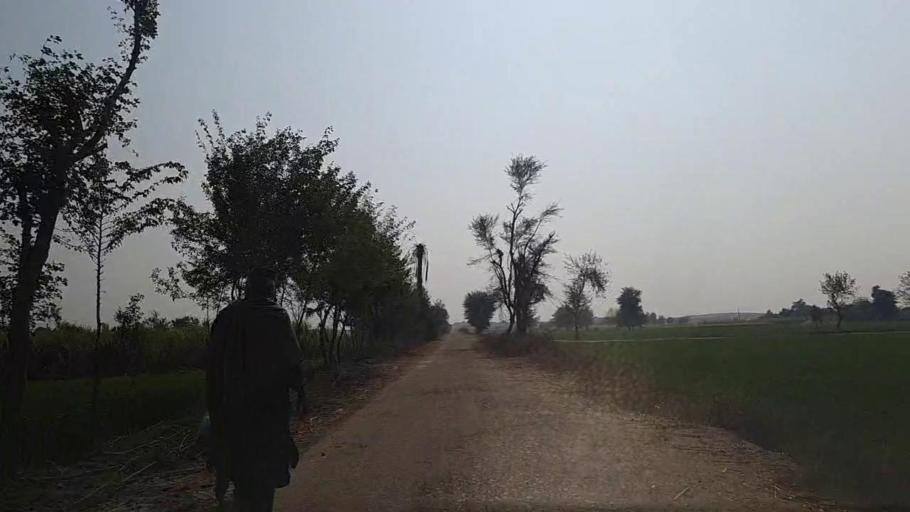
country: PK
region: Sindh
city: Jam Sahib
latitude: 26.4547
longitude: 68.5235
